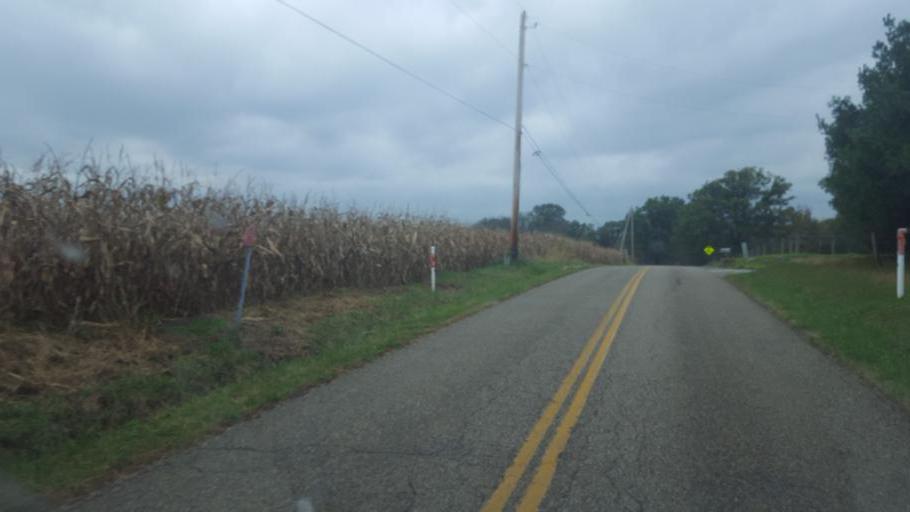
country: US
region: Ohio
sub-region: Carroll County
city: Carrollton
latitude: 40.5332
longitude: -81.1556
